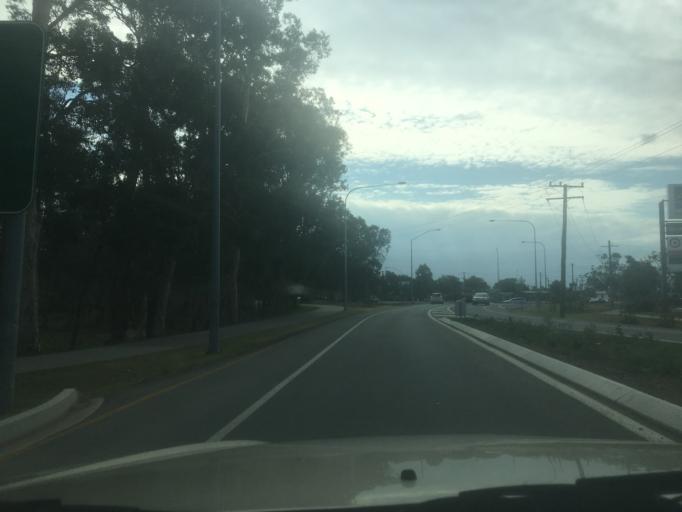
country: AU
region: Queensland
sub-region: Moreton Bay
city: Bongaree
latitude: -27.0649
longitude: 153.1564
